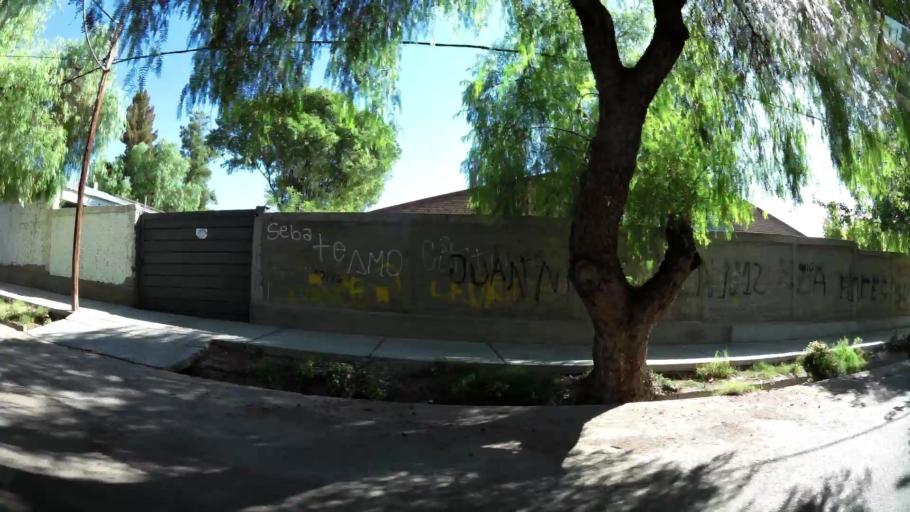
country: AR
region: Mendoza
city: Mendoza
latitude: -32.8744
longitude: -68.8695
